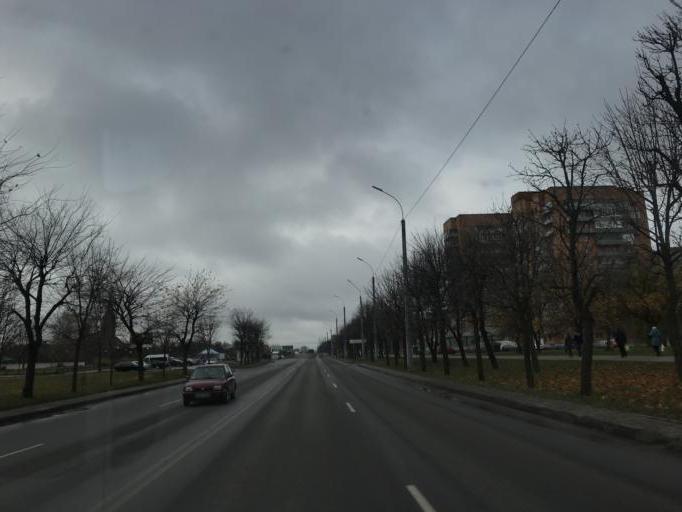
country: BY
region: Mogilev
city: Mahilyow
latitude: 53.8719
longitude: 30.3265
